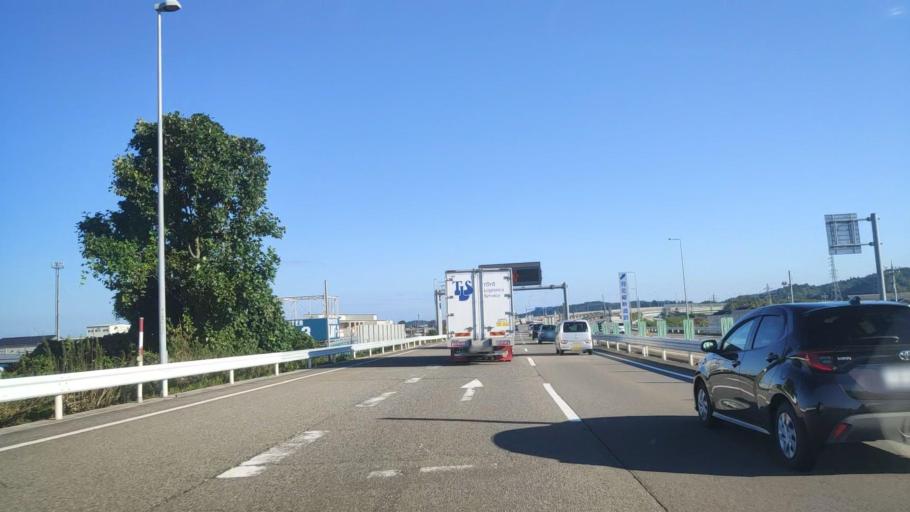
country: JP
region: Ishikawa
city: Tsubata
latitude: 36.6793
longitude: 136.7228
